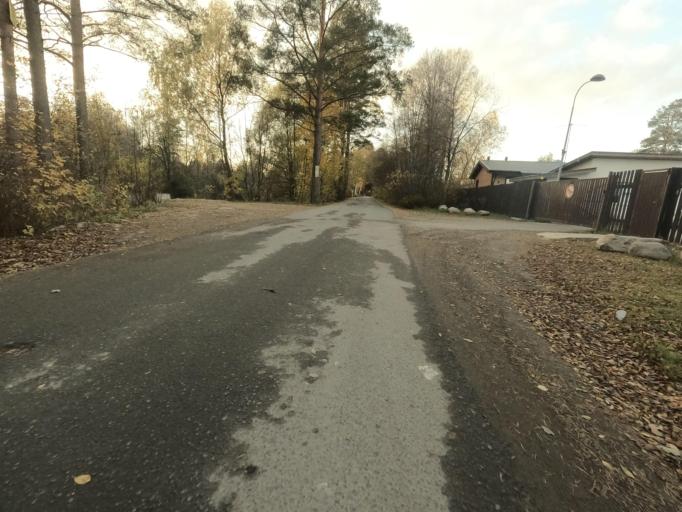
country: RU
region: St.-Petersburg
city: Beloostrov
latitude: 60.1615
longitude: 30.0036
